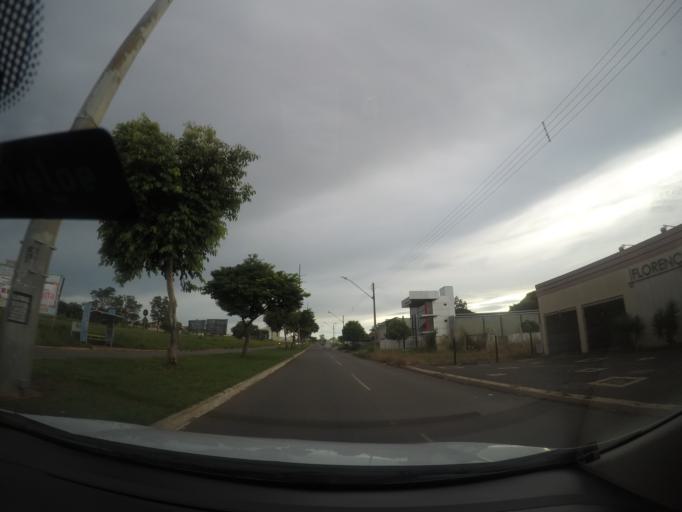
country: BR
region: Goias
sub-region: Goiania
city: Goiania
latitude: -16.7402
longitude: -49.3138
